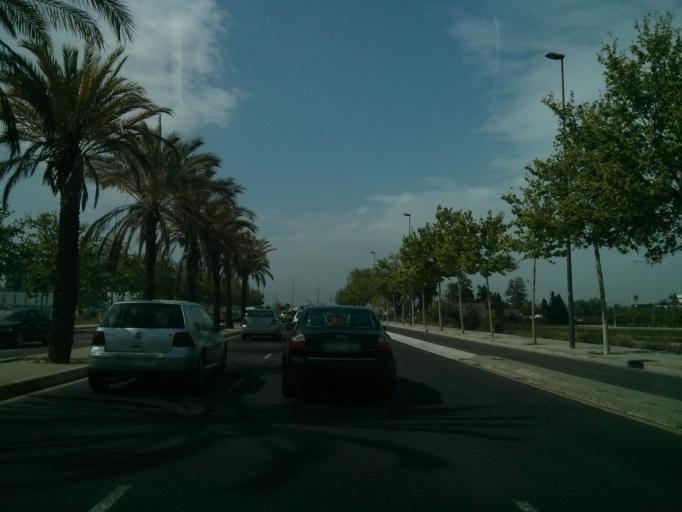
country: ES
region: Valencia
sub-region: Provincia de Valencia
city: Alboraya
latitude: 39.4920
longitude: -0.3556
